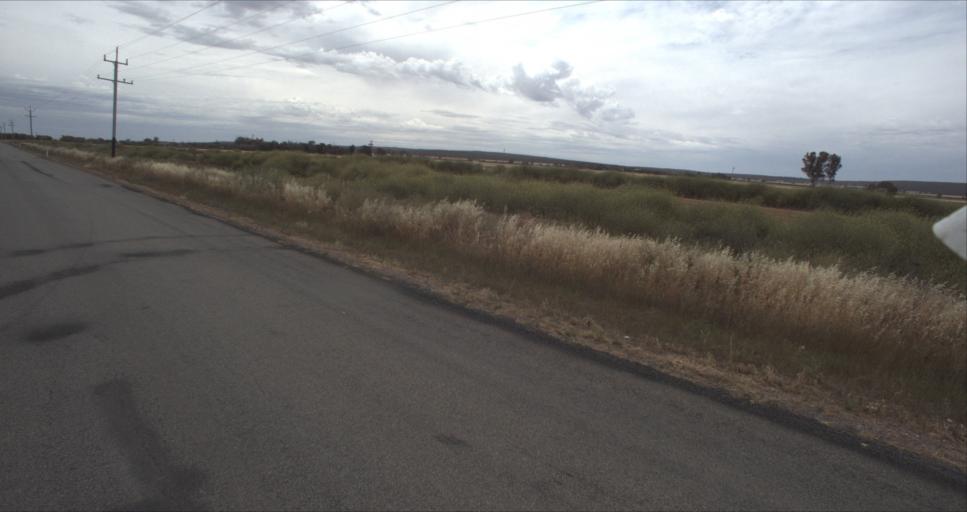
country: AU
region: New South Wales
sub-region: Leeton
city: Leeton
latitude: -34.4813
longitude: 146.4002
